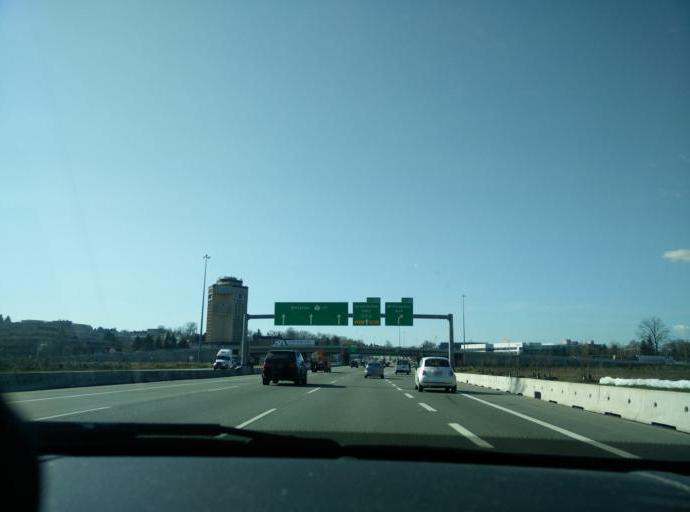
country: CA
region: British Columbia
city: Burnaby
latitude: 49.2578
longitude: -123.0004
